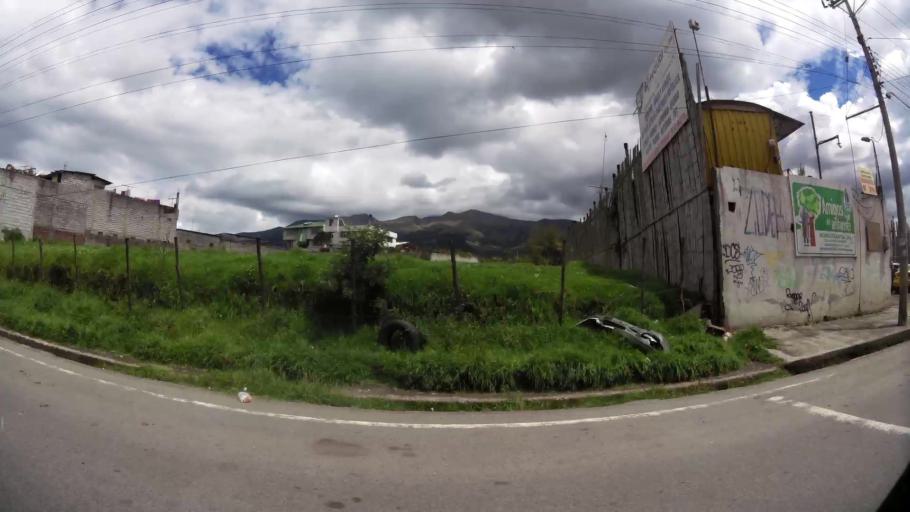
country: EC
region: Pichincha
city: Sangolqui
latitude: -0.3539
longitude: -78.5494
